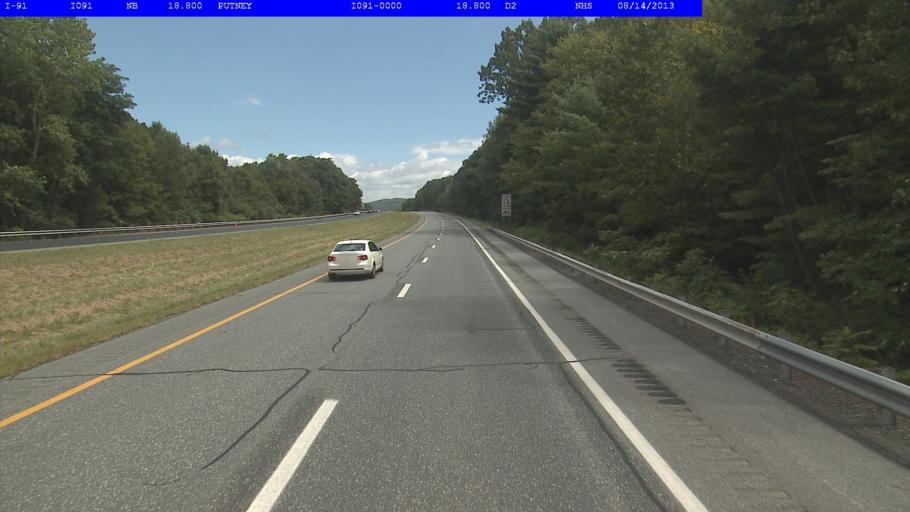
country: US
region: New Hampshire
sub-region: Cheshire County
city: Westmoreland
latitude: 42.9662
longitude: -72.5083
